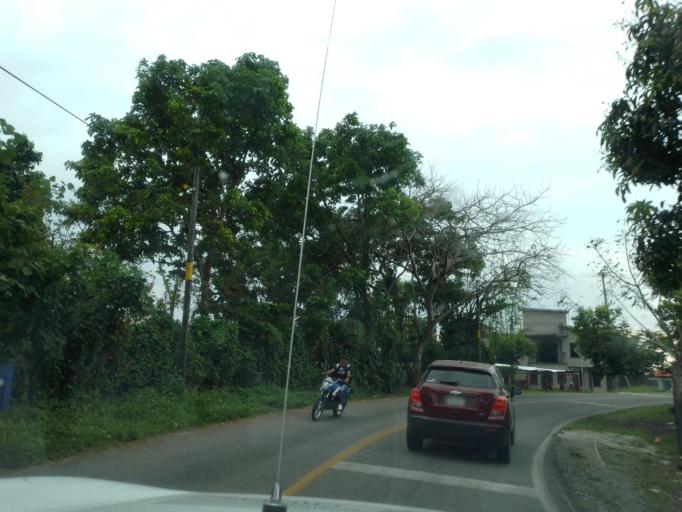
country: MX
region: Chiapas
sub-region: Union Juarez
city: Santo Domingo
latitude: 15.0417
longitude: -92.1366
